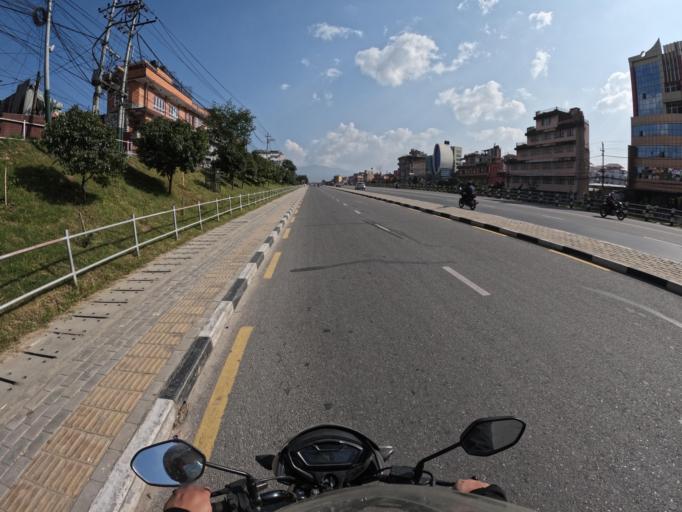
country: NP
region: Central Region
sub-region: Bagmati Zone
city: Patan
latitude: 27.6709
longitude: 85.3050
